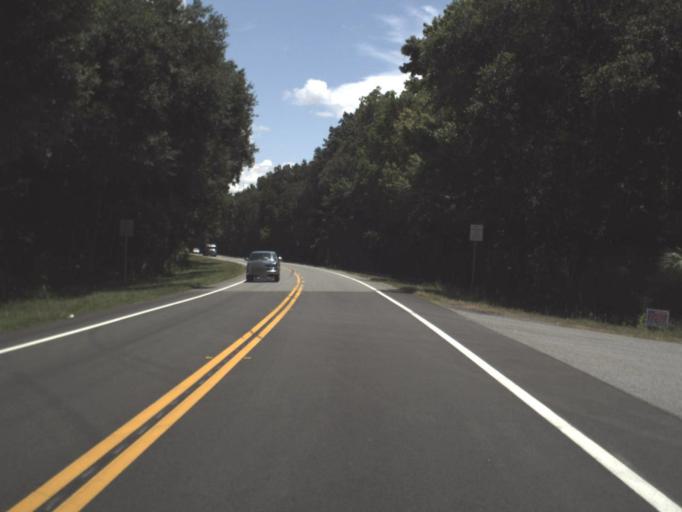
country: US
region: Florida
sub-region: Leon County
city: Woodville
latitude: 30.1437
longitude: -83.9667
